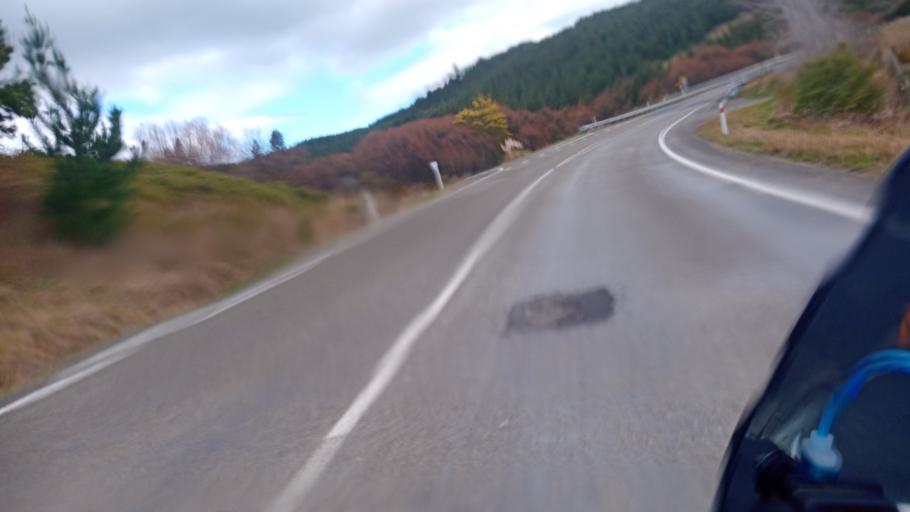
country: NZ
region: Gisborne
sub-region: Gisborne District
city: Gisborne
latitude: -38.0517
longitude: 178.2979
